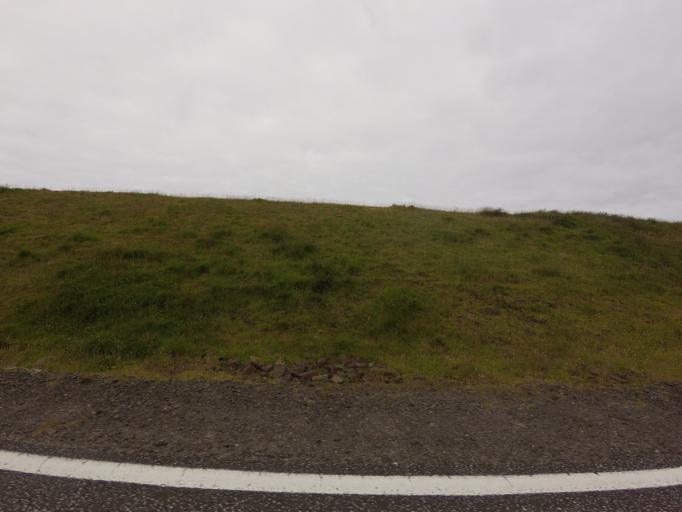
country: FO
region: Suduroy
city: Tvoroyri
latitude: 61.5313
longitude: -6.7987
